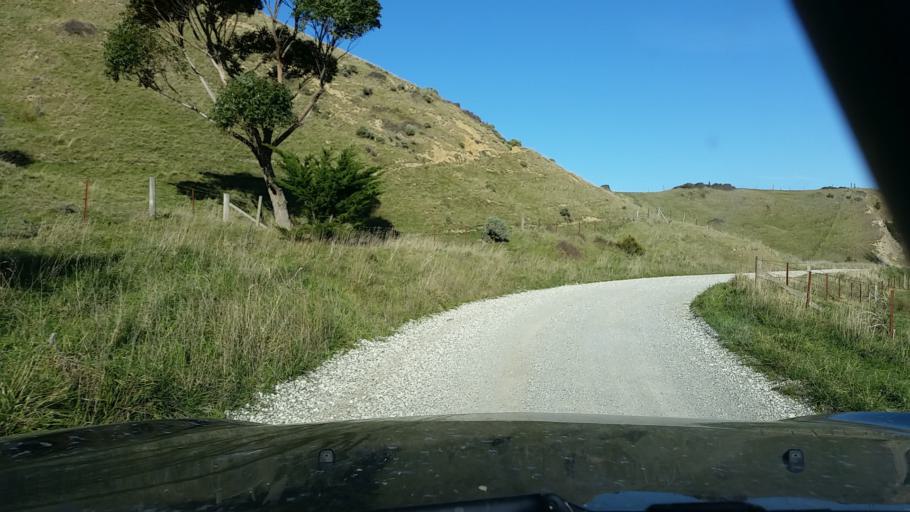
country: NZ
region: Marlborough
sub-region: Marlborough District
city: Blenheim
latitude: -41.8399
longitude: 174.1816
